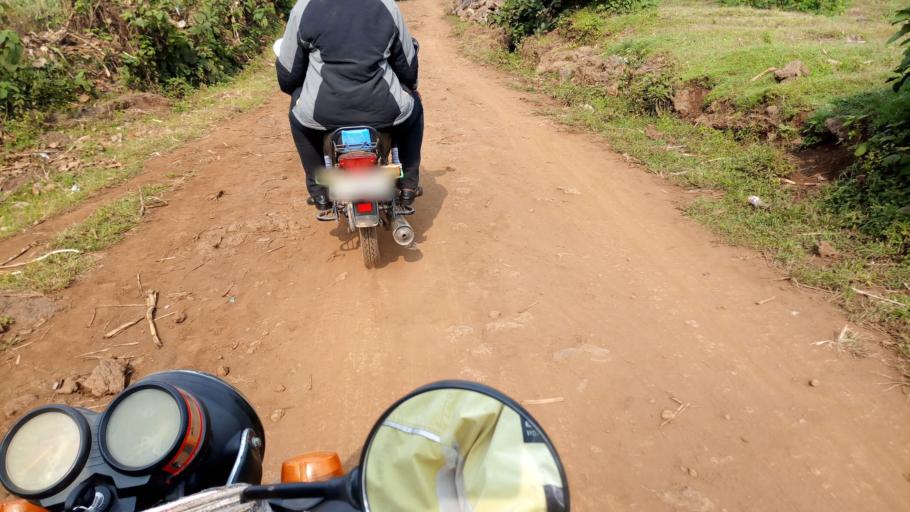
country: UG
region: Western Region
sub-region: Kisoro District
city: Kisoro
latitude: -1.3105
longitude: 29.6568
